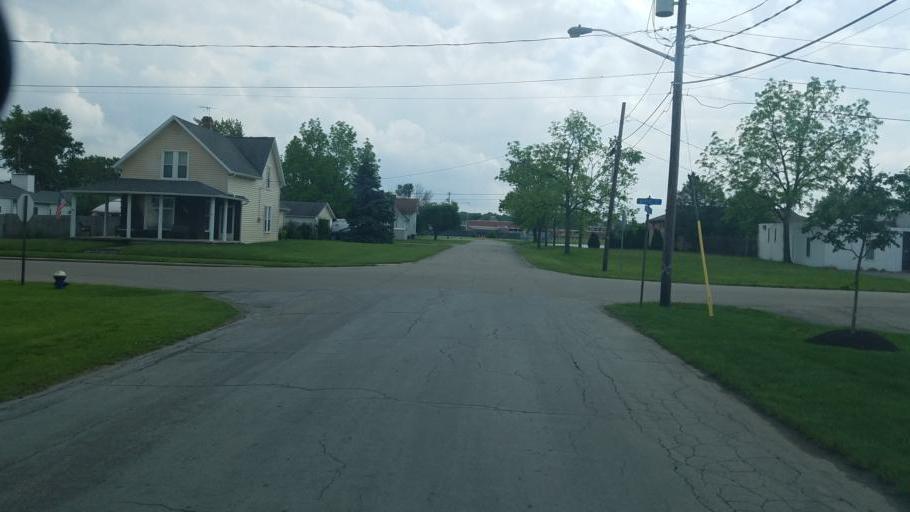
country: US
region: Ohio
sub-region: Franklin County
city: Hilliard
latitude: 40.0342
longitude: -83.1612
